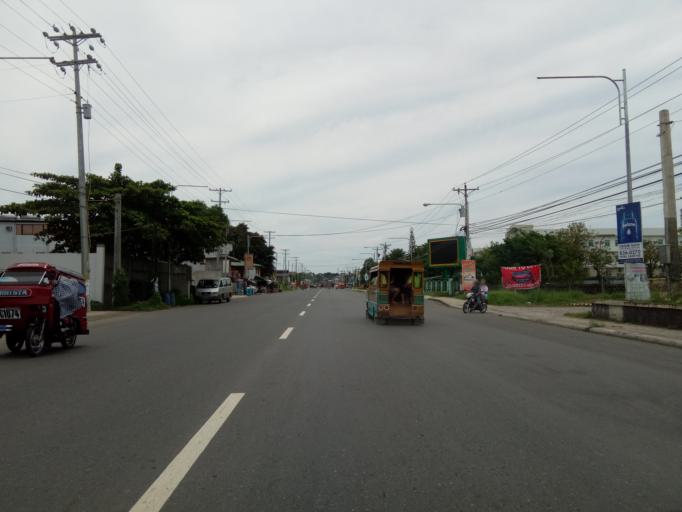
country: PH
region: Caraga
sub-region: Province of Surigao del Norte
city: Rizal
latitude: 9.7652
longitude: 125.4832
